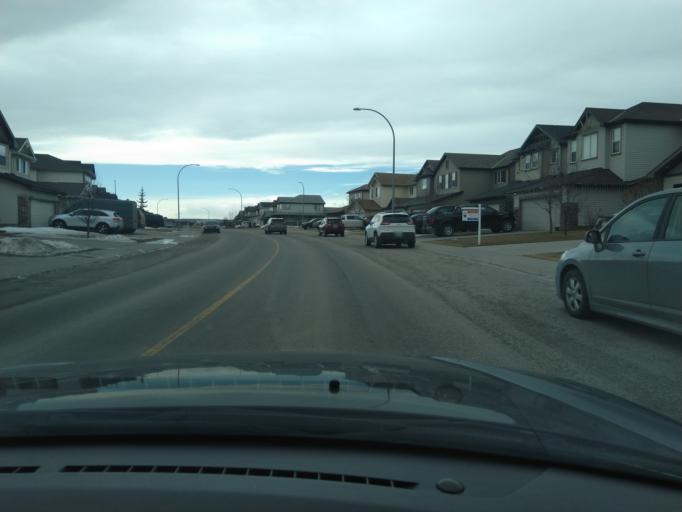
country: CA
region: Alberta
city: Calgary
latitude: 51.1711
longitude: -114.0498
